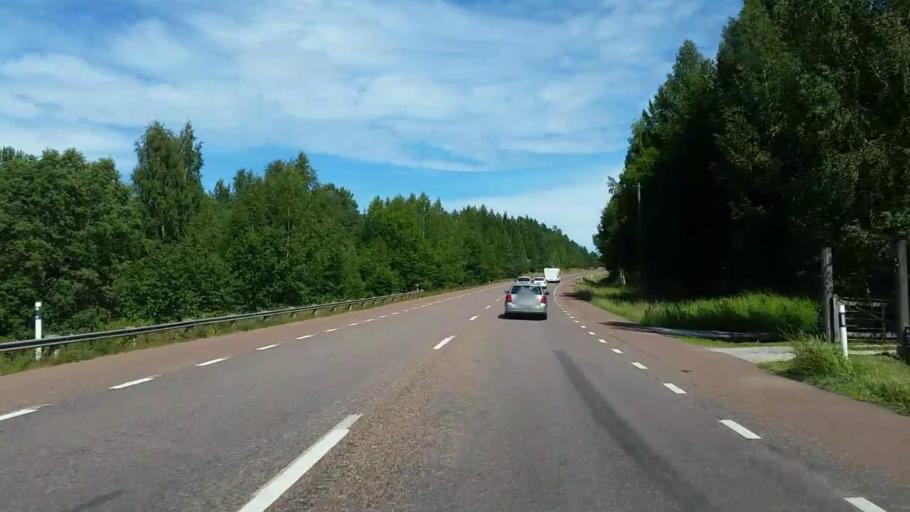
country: SE
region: Dalarna
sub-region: Rattviks Kommun
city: Raettvik
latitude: 60.9220
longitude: 15.2106
